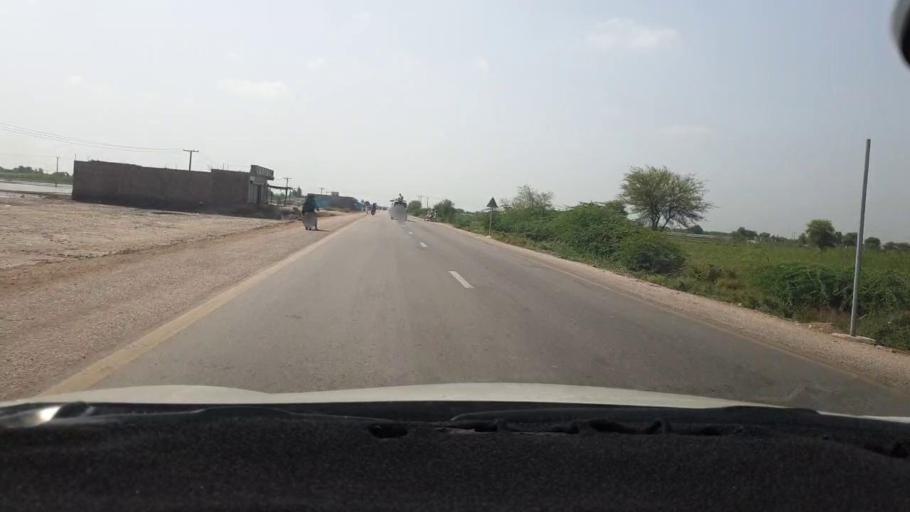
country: PK
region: Sindh
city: Mirpur Khas
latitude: 25.6087
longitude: 69.0831
